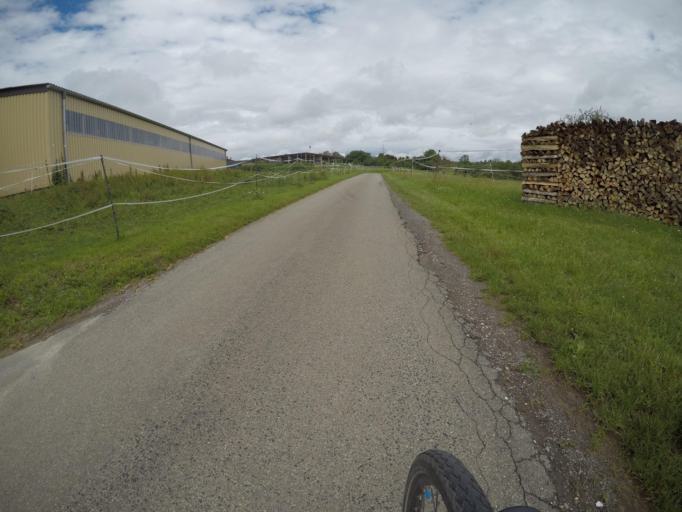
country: DE
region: Baden-Wuerttemberg
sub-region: Regierungsbezirk Stuttgart
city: Gartringen
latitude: 48.6459
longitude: 8.8840
